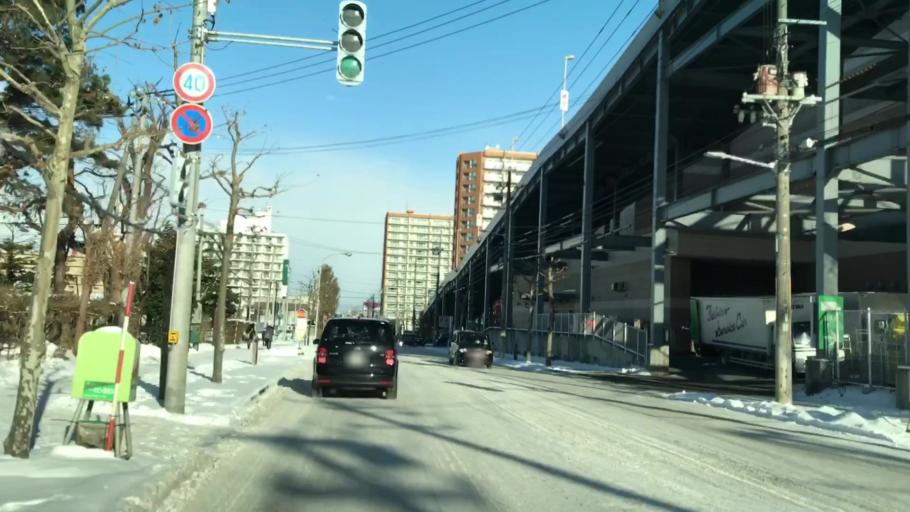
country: JP
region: Hokkaido
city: Sapporo
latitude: 43.0965
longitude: 141.2753
